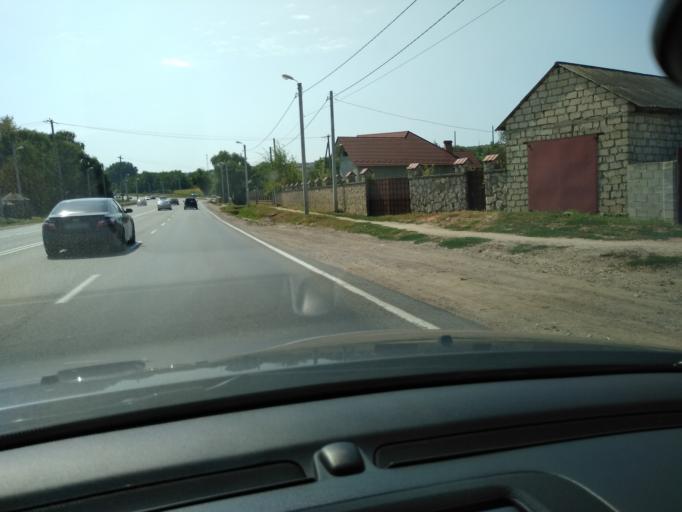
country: MD
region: Chisinau
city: Cricova
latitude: 47.2382
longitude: 28.7629
